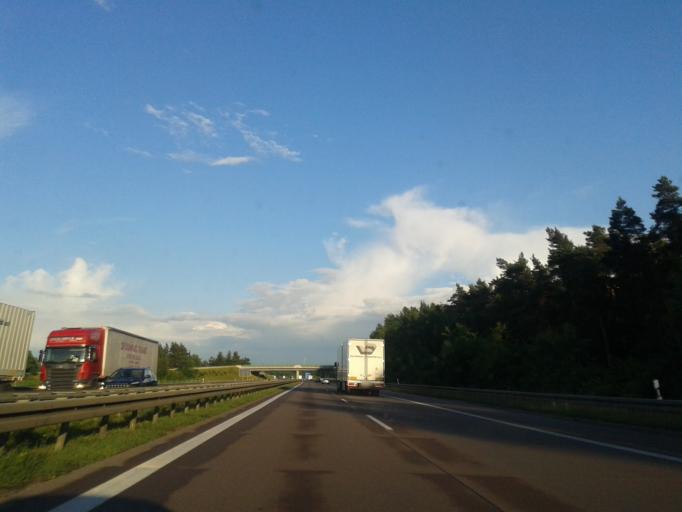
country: DE
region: Saxony
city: Naunhof
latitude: 51.2943
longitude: 12.6223
